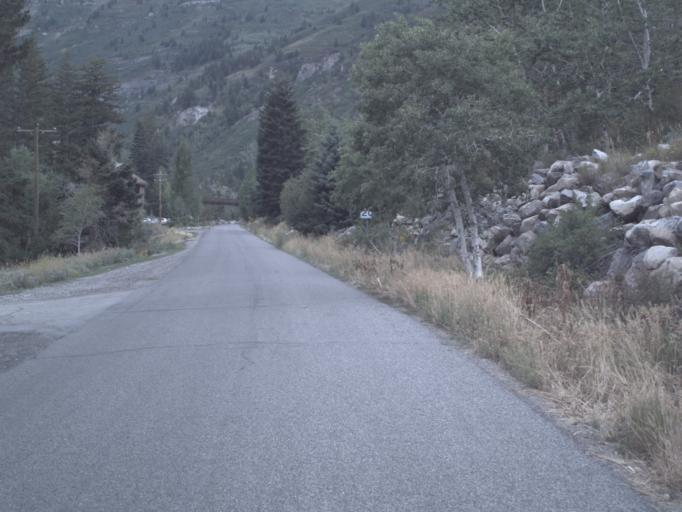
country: US
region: Utah
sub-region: Utah County
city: Lindon
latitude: 40.4042
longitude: -111.5987
